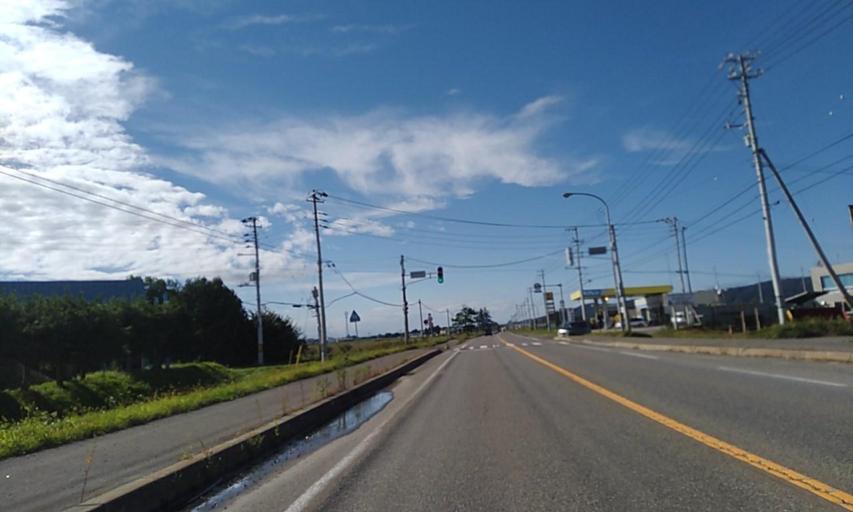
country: JP
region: Hokkaido
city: Obihiro
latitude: 42.9129
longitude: 143.3505
